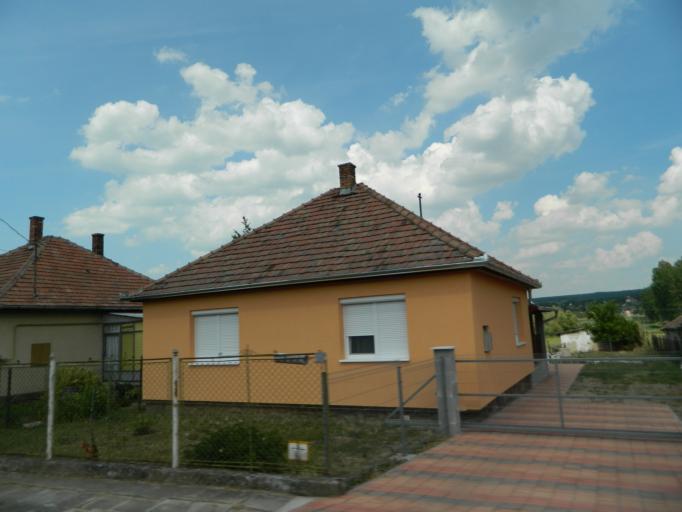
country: HU
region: Somogy
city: Balatonfoldvar
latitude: 46.8358
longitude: 17.8879
